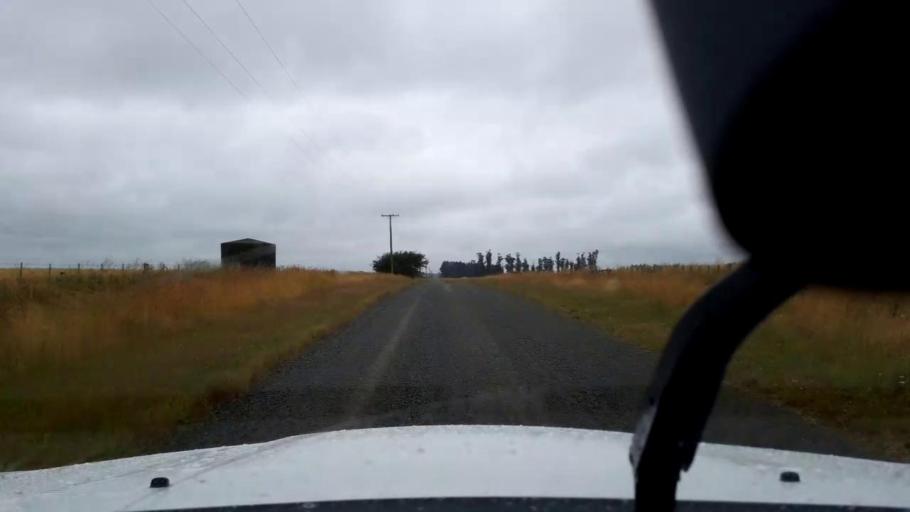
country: NZ
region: Canterbury
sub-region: Timaru District
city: Pleasant Point
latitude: -44.2322
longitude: 171.2025
